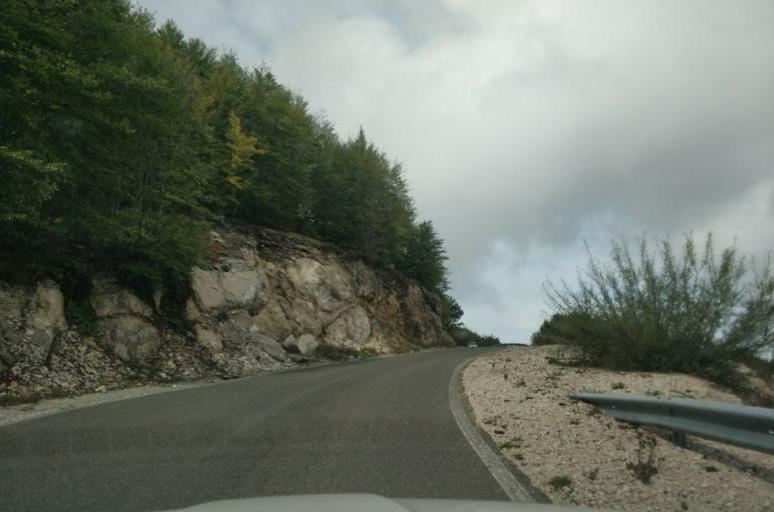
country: AL
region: Durres
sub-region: Rrethi i Krujes
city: Kruje
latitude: 41.5178
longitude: 19.8067
